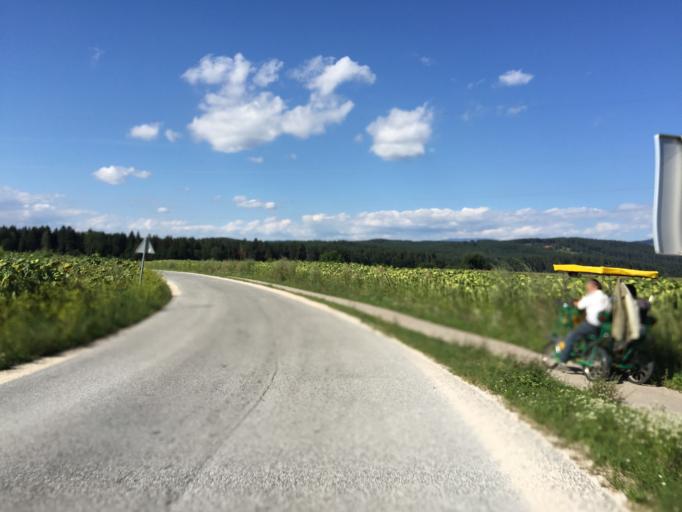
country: AT
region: Carinthia
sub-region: Politischer Bezirk Volkermarkt
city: Feistritz ob Bleiburg
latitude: 46.5694
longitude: 14.7559
